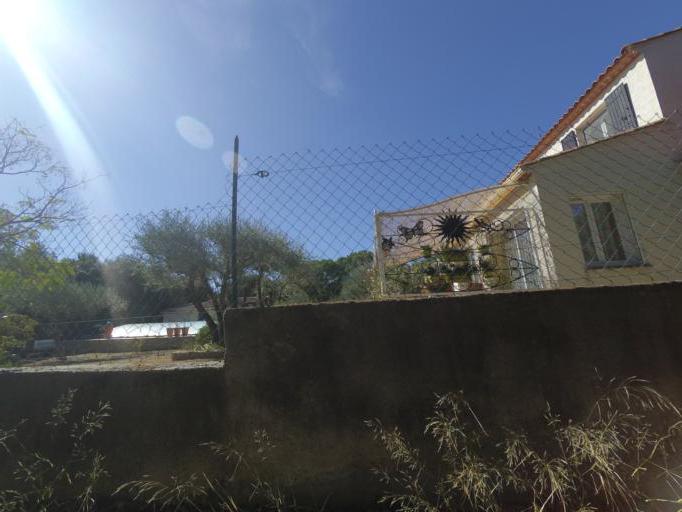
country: FR
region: Languedoc-Roussillon
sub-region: Departement du Gard
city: Nages-et-Solorgues
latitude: 43.7705
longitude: 4.2393
